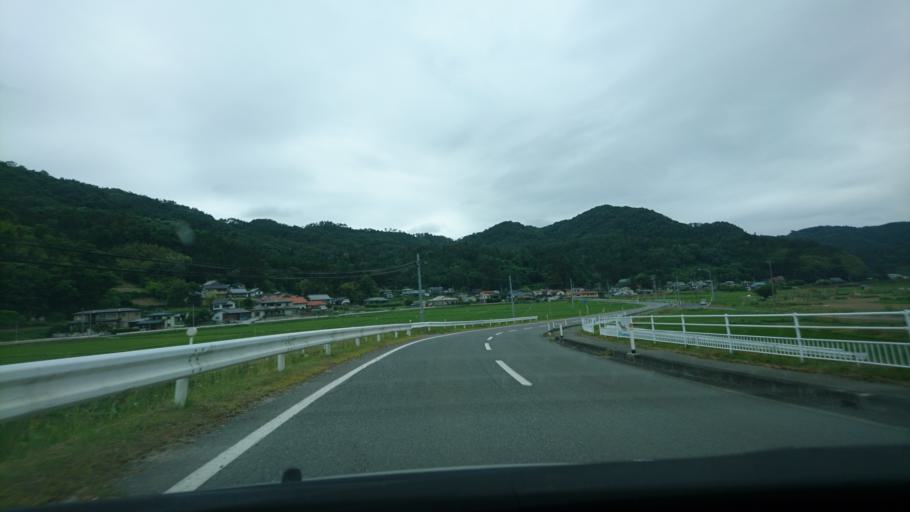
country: JP
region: Iwate
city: Ichinoseki
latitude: 38.9616
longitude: 141.2444
